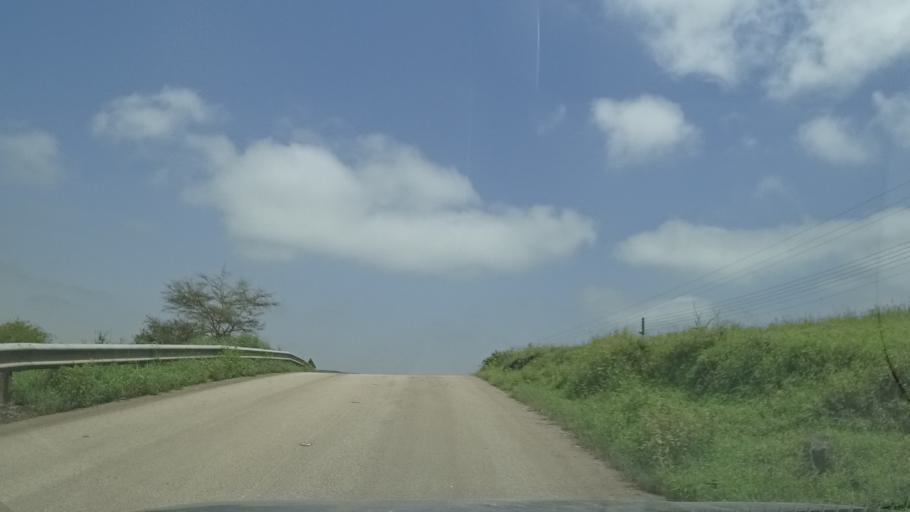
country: OM
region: Zufar
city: Salalah
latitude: 17.2208
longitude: 54.2032
